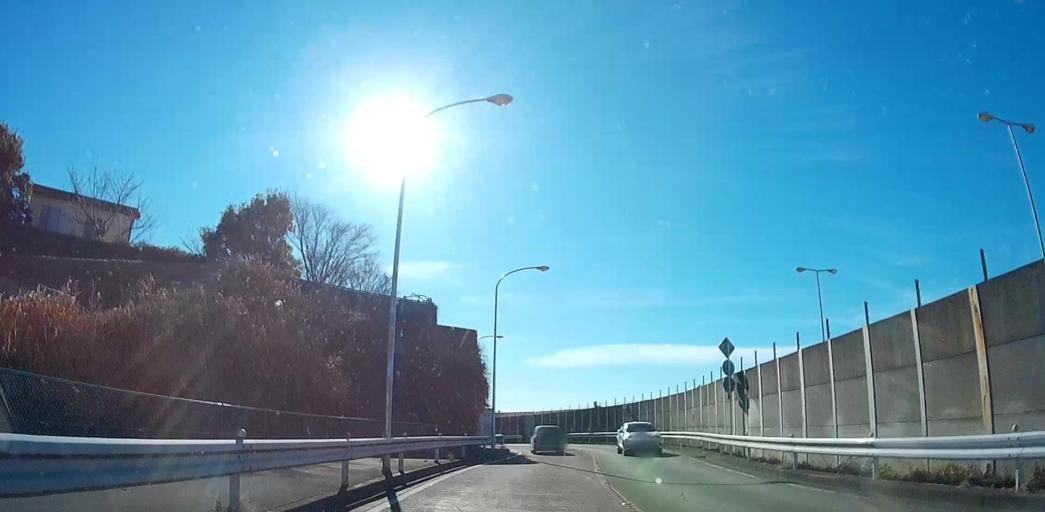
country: JP
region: Chiba
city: Narita
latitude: 35.7610
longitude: 140.3921
